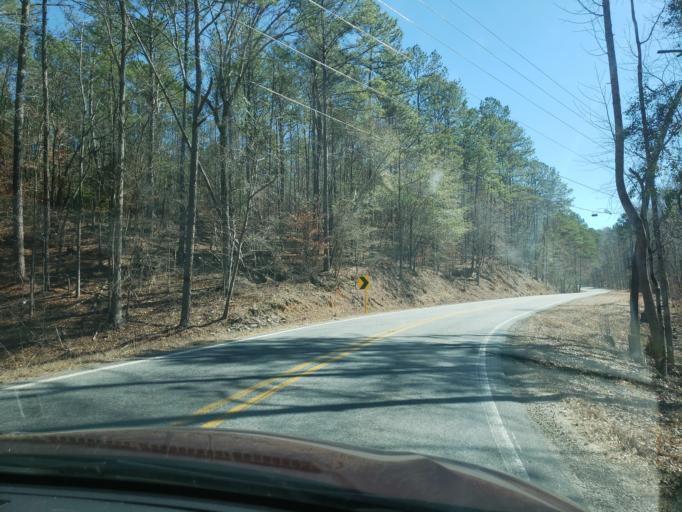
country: US
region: Alabama
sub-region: Elmore County
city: Tallassee
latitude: 32.6756
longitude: -85.8984
